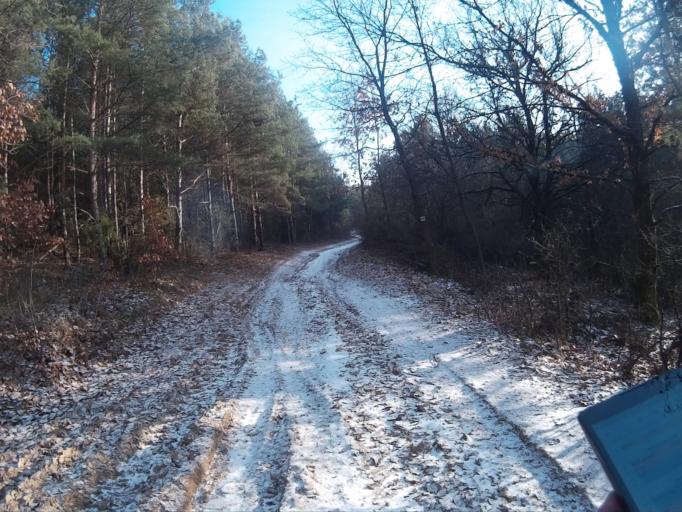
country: HU
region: Borsod-Abauj-Zemplen
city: Szendro
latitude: 48.4834
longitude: 20.8263
